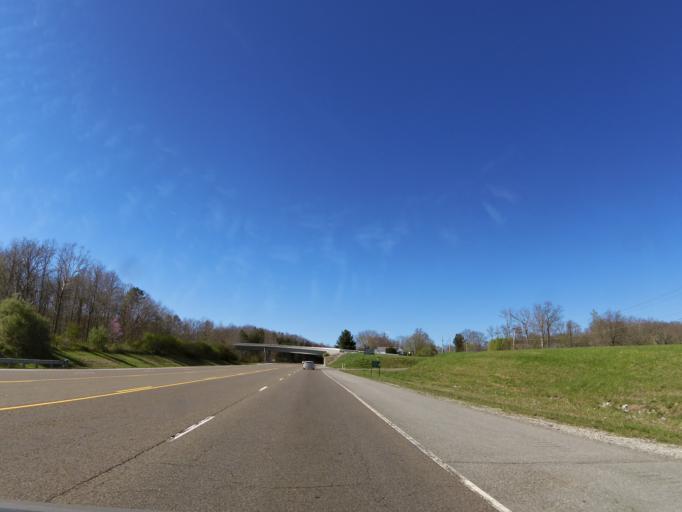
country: US
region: Tennessee
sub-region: Scott County
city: Oneida
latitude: 36.4567
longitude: -84.5465
